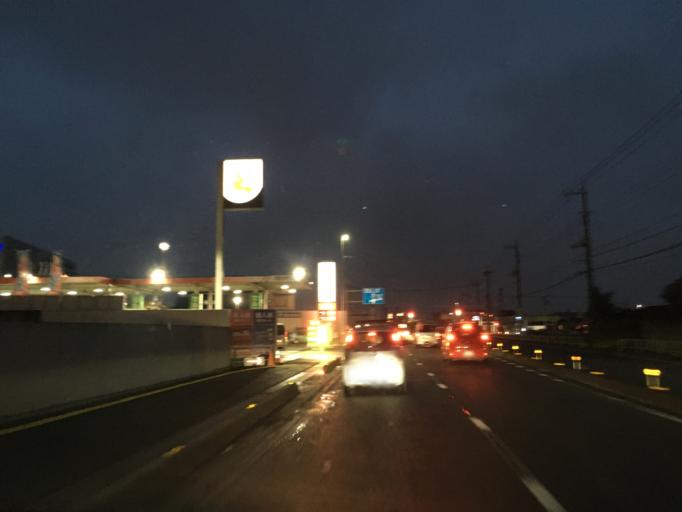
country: JP
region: Saitama
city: Shiki
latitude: 35.8081
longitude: 139.5502
